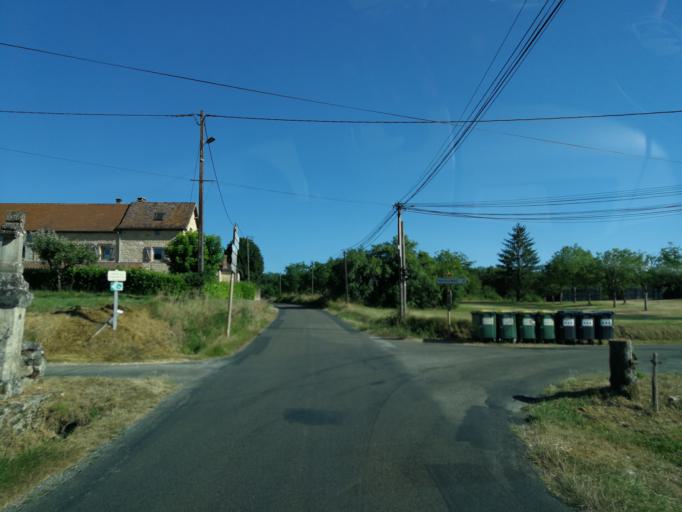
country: FR
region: Midi-Pyrenees
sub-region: Departement du Lot
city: Gourdon
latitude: 44.7771
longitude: 1.3654
